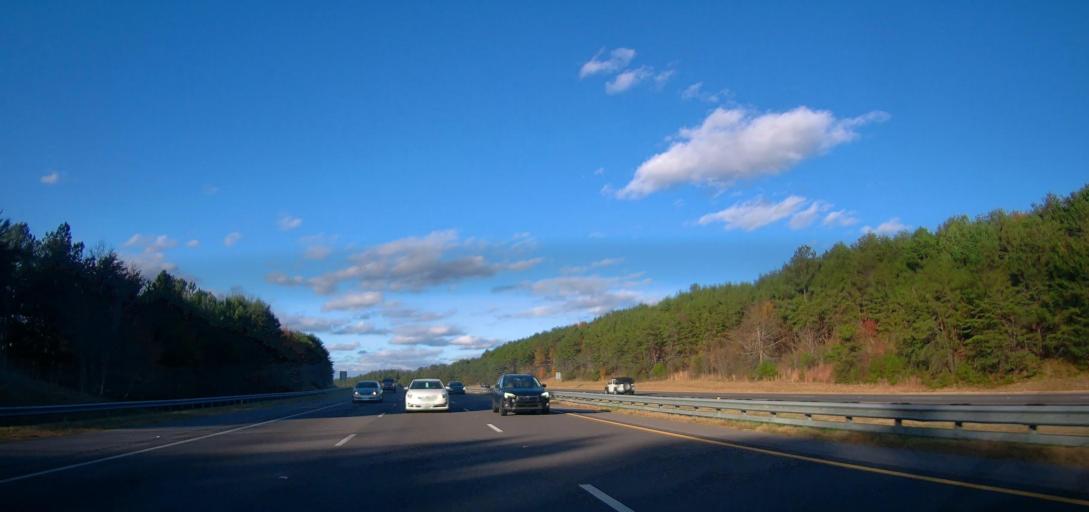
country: US
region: Alabama
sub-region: Jefferson County
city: Morris
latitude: 33.7274
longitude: -86.8249
